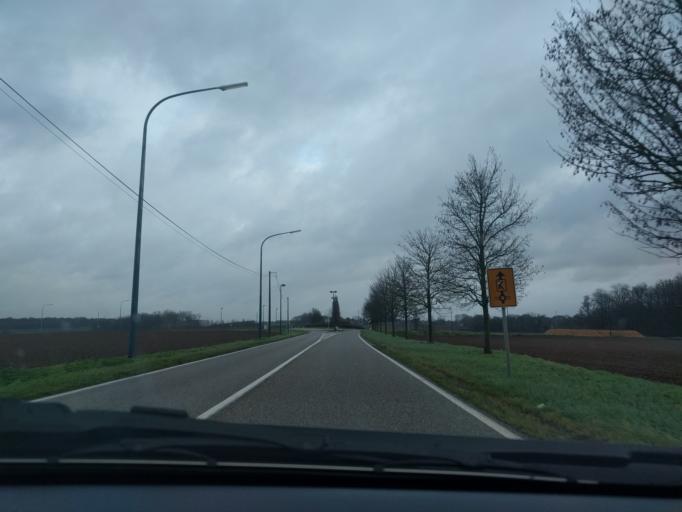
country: BE
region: Wallonia
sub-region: Province de Namur
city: Noville-les-Bois
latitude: 50.5156
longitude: 4.9821
